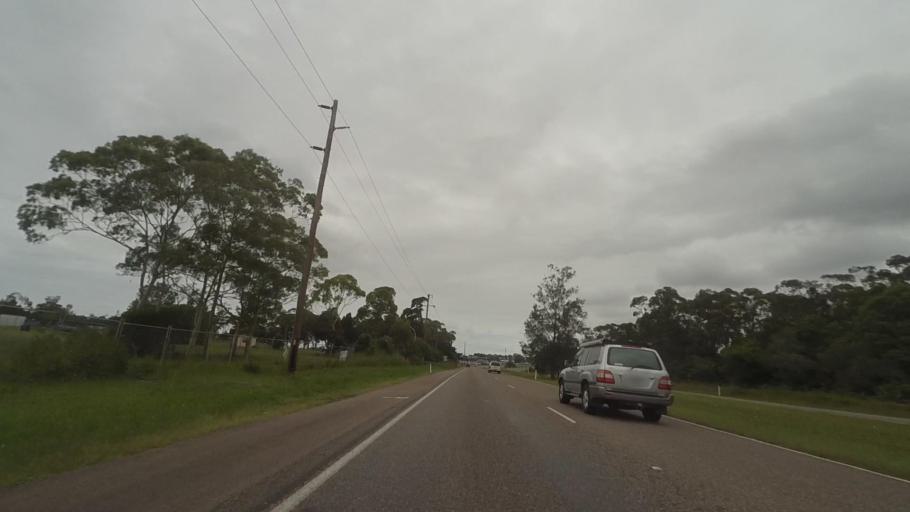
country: AU
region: New South Wales
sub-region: Wyong Shire
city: Buff Point
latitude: -33.1933
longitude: 151.5271
